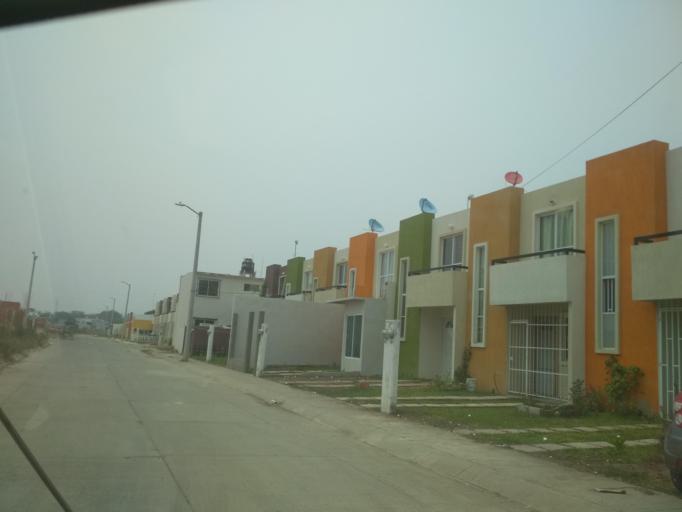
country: MX
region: Veracruz
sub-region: Veracruz
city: Las Amapolas
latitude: 19.1539
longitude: -96.2179
